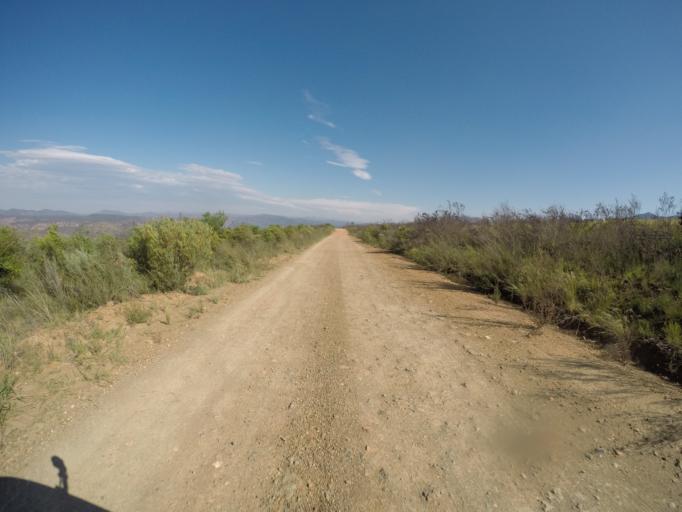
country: ZA
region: Eastern Cape
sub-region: Cacadu District Municipality
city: Kareedouw
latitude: -33.6349
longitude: 24.4710
